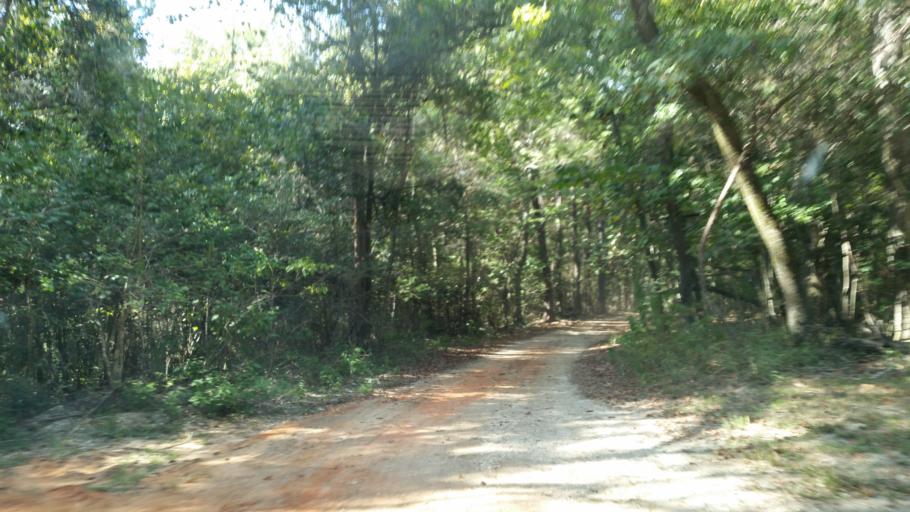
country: US
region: Alabama
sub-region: Baldwin County
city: Spanish Fort
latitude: 30.7409
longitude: -87.9197
